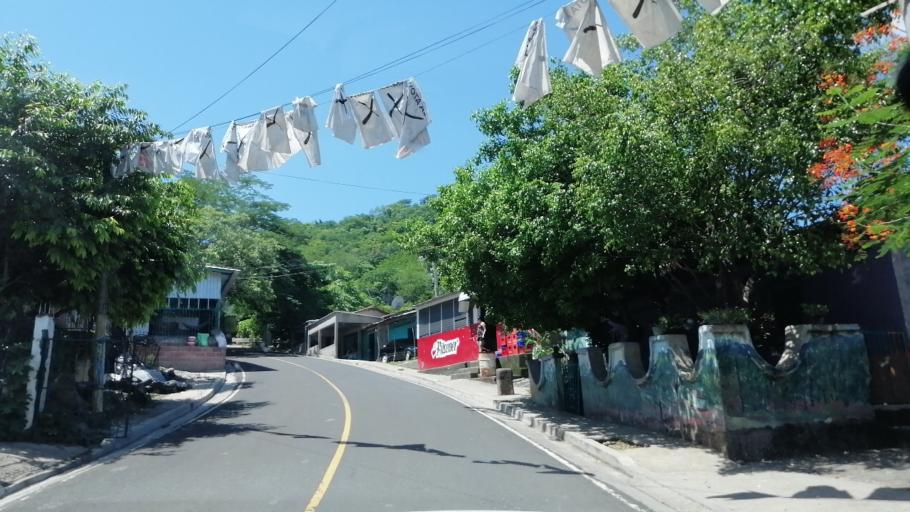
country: SV
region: San Miguel
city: Sesori
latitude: 13.8080
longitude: -88.4022
